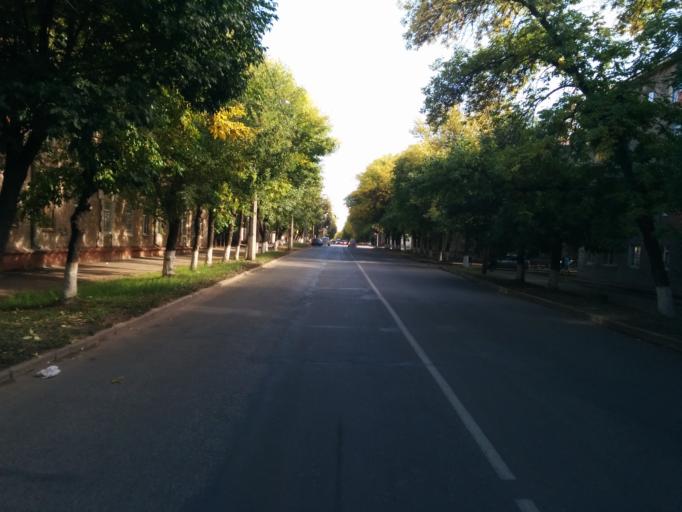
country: RU
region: Bashkortostan
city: Ufa
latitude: 54.8237
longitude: 56.0657
